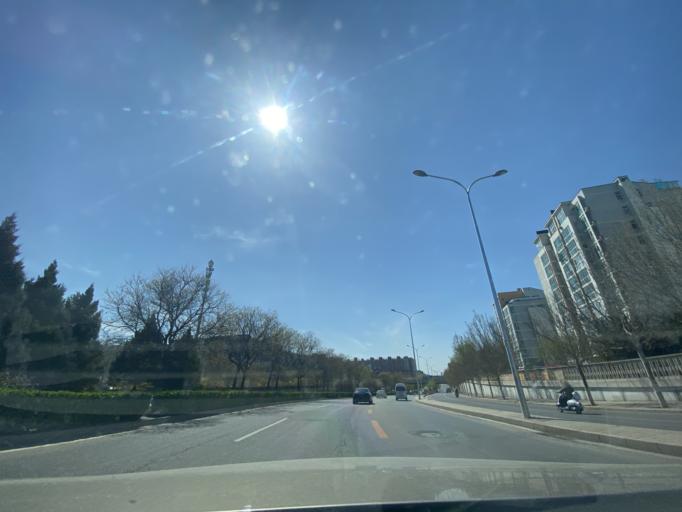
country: CN
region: Beijing
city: Sijiqing
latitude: 39.9330
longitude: 116.2466
